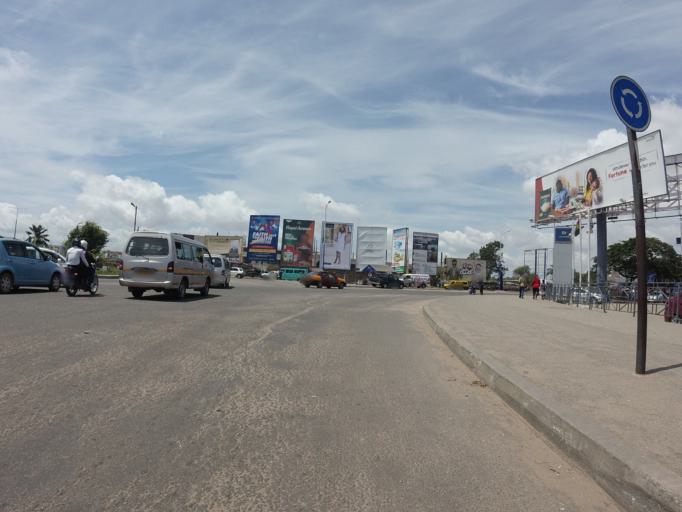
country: GH
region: Greater Accra
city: Accra
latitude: 5.5614
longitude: -0.2290
